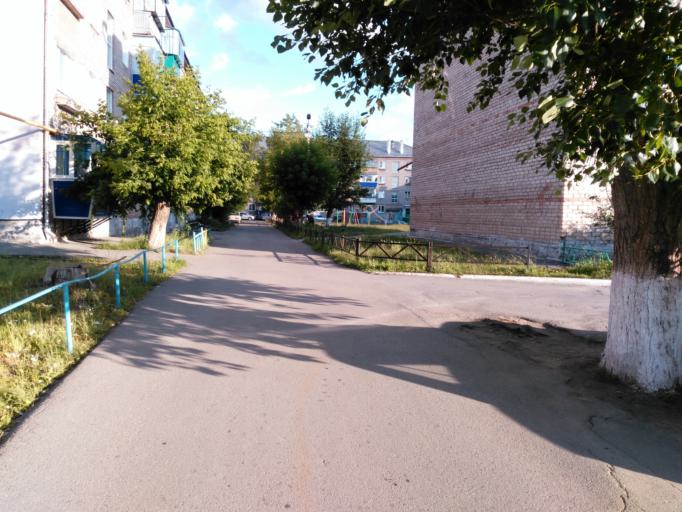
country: RU
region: Bashkortostan
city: Uchaly
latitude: 54.3164
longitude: 59.3841
